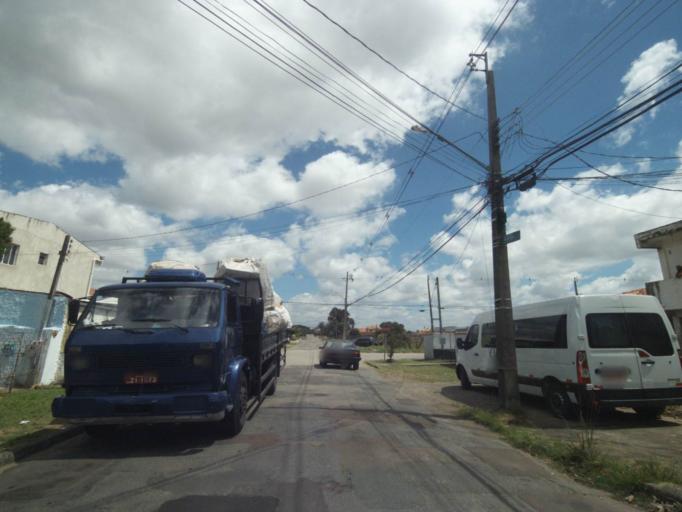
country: BR
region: Parana
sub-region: Pinhais
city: Pinhais
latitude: -25.4405
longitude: -49.2066
